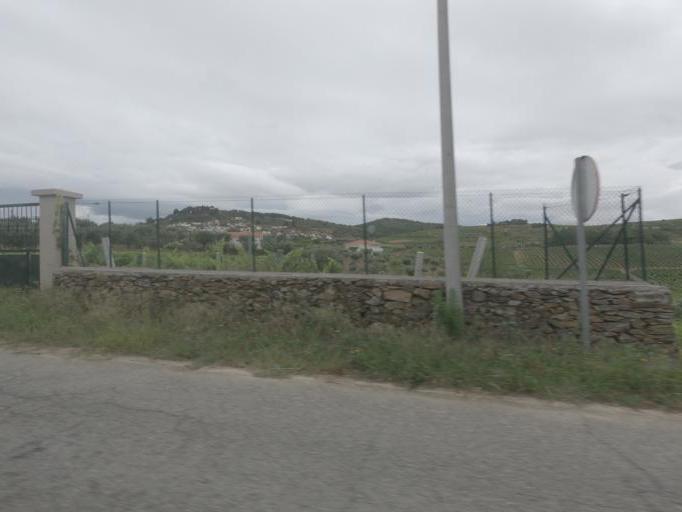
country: PT
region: Vila Real
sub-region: Sabrosa
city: Sabrosa
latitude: 41.2865
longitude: -7.5290
